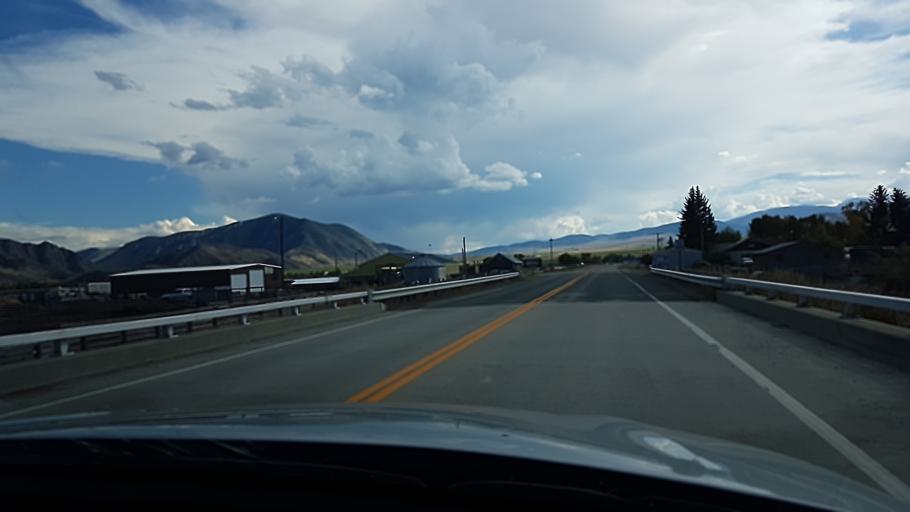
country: US
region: Montana
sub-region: Jefferson County
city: Whitehall
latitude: 45.8684
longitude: -111.9543
